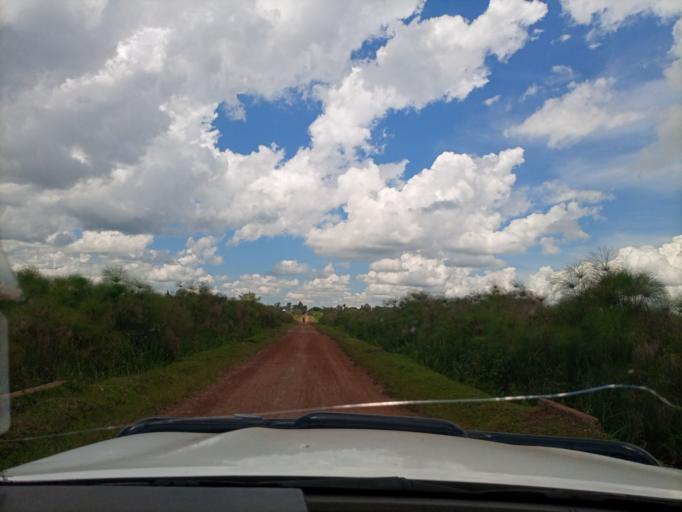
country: UG
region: Eastern Region
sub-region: Tororo District
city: Tororo
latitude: 0.6362
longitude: 33.9928
